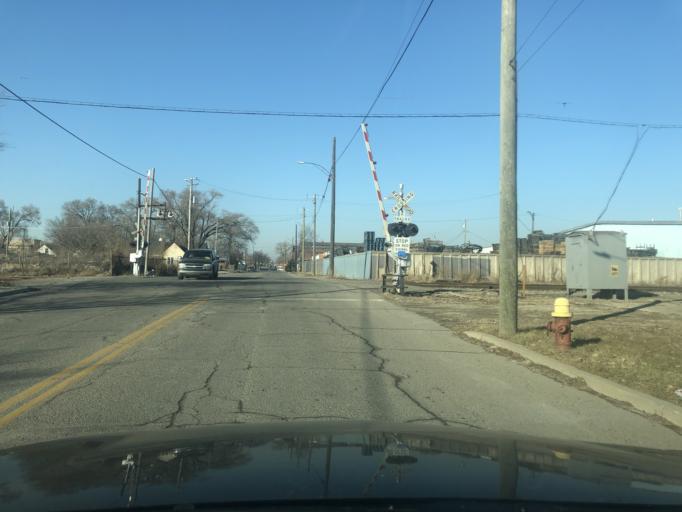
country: US
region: Michigan
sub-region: Wayne County
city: River Rouge
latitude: 42.3070
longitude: -83.0940
